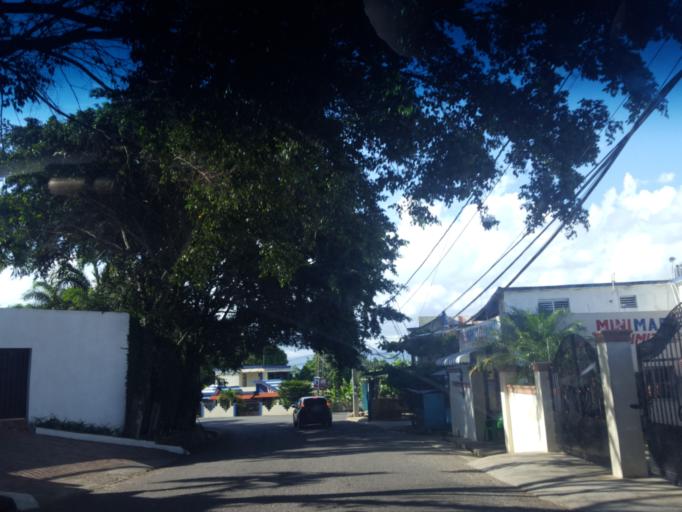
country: DO
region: La Vega
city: Rio Verde Arriba
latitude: 19.3542
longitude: -70.6034
